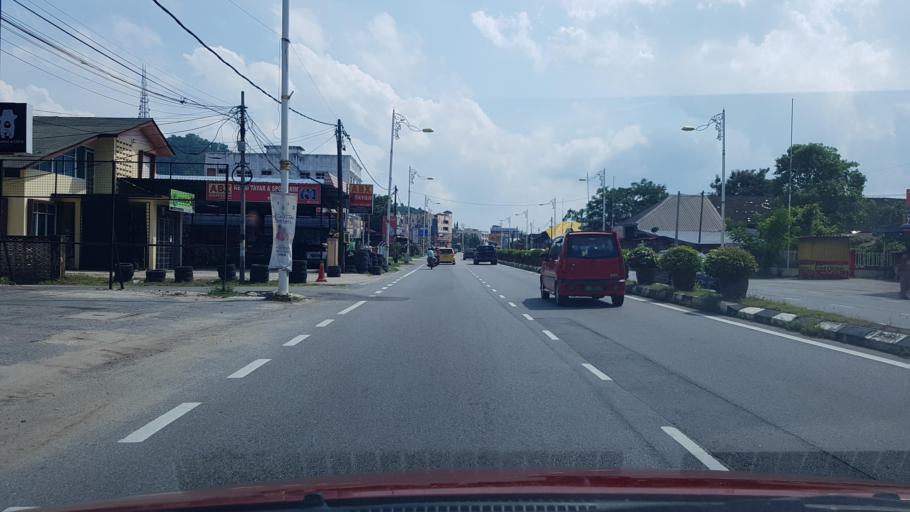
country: MY
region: Terengganu
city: Kuala Terengganu
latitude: 5.3135
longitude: 103.1417
